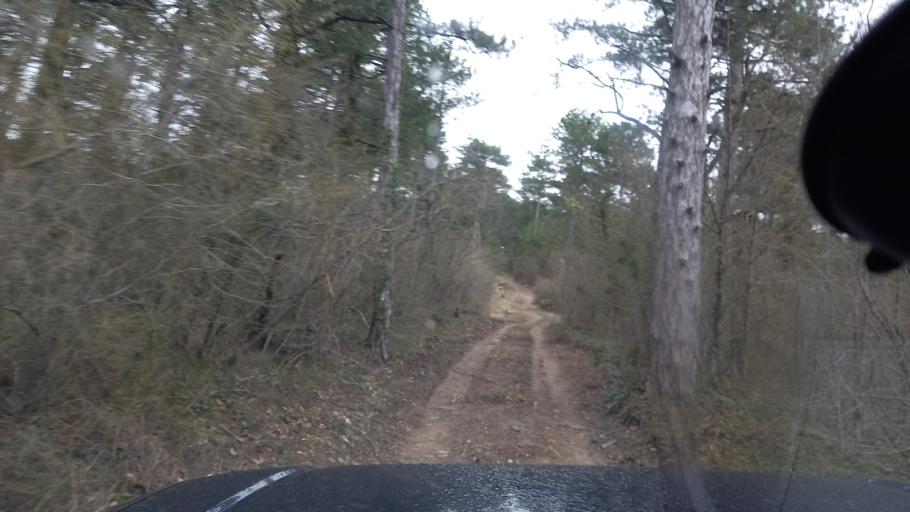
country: RU
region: Krasnodarskiy
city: Arkhipo-Osipovka
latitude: 44.3719
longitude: 38.4729
